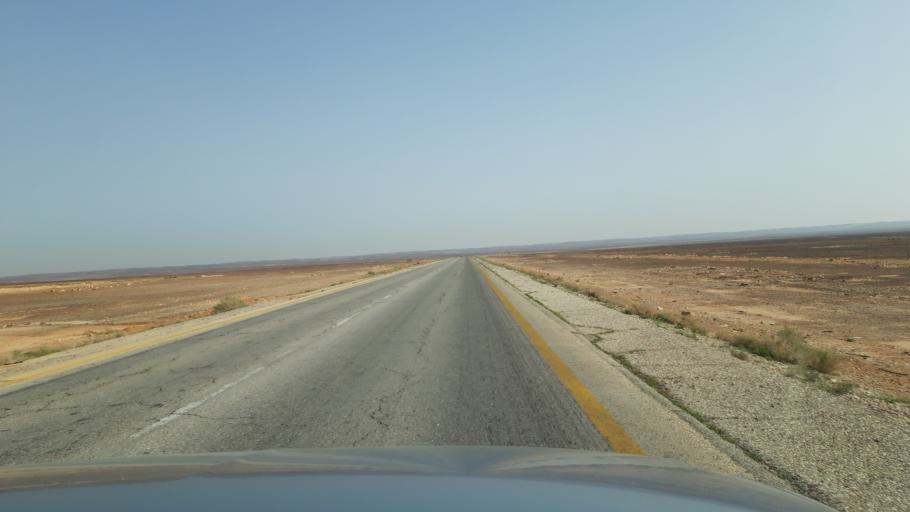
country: JO
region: Amman
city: Al Azraq ash Shamali
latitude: 31.8073
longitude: 36.5935
